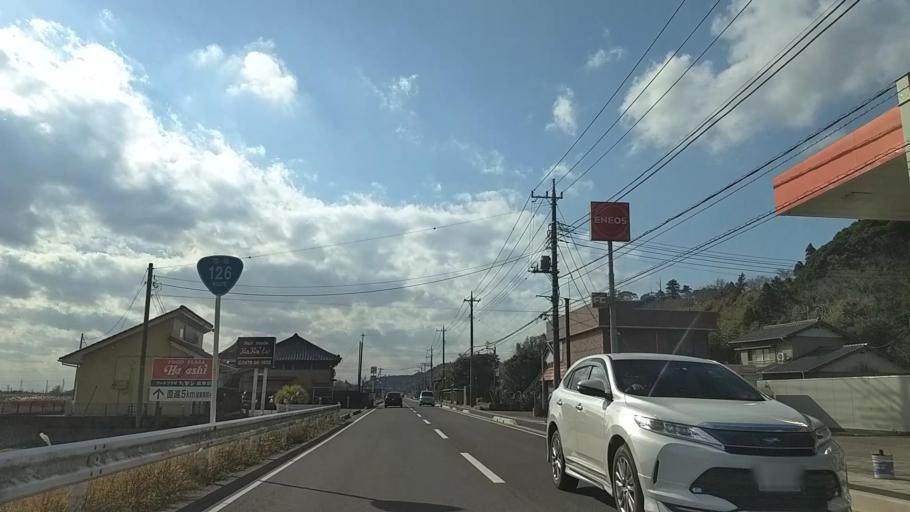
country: JP
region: Chiba
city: Naruto
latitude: 35.6286
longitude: 140.4467
